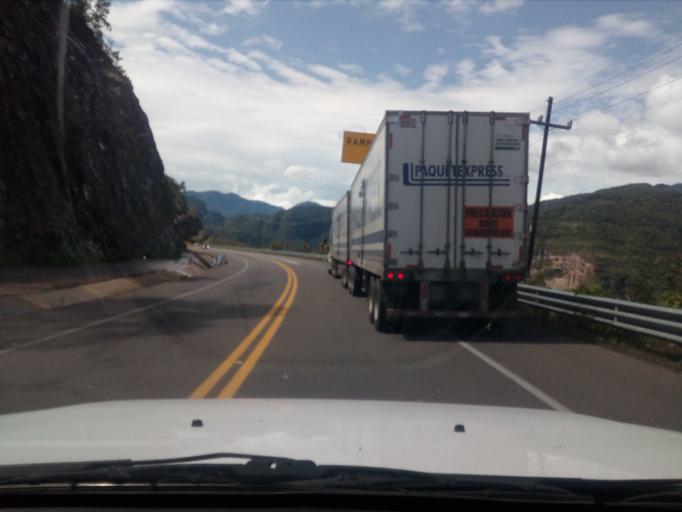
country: MX
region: Durango
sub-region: Pueblo Nuevo
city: La Ciudad
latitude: 23.6225
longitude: -105.6846
